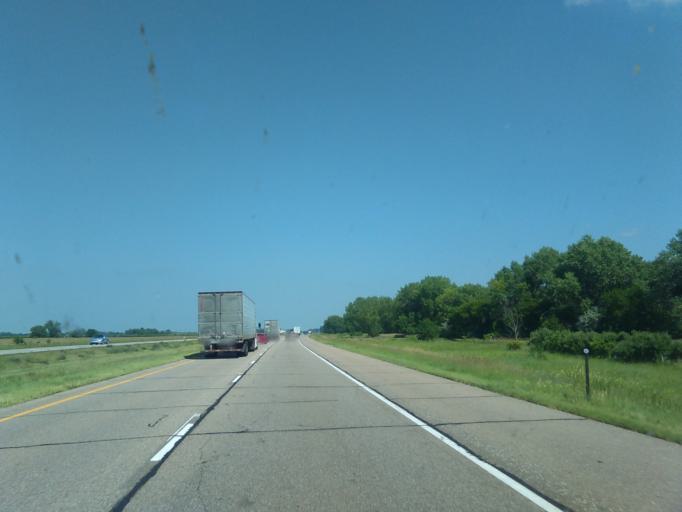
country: US
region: Nebraska
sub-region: Buffalo County
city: Kearney
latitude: 40.6726
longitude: -99.1788
